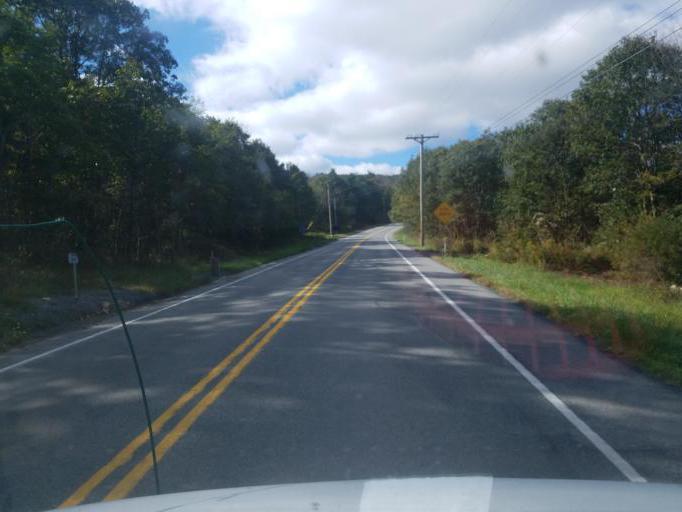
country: US
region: Pennsylvania
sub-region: Bedford County
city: Earlston
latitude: 40.0159
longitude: -78.1945
